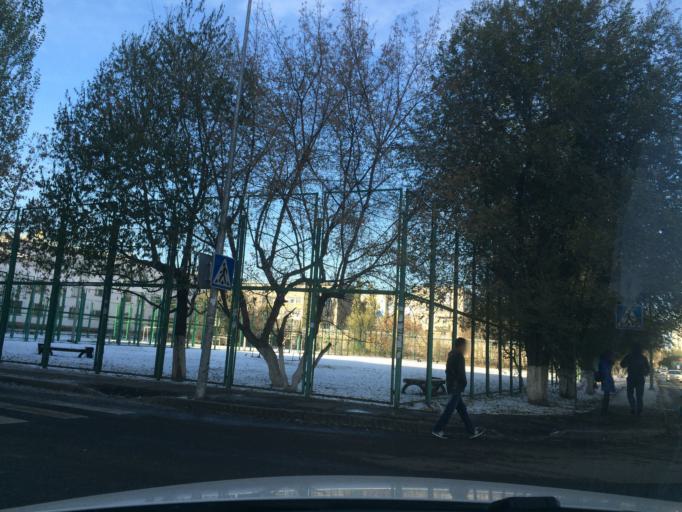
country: KZ
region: Astana Qalasy
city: Astana
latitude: 51.1592
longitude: 71.4330
